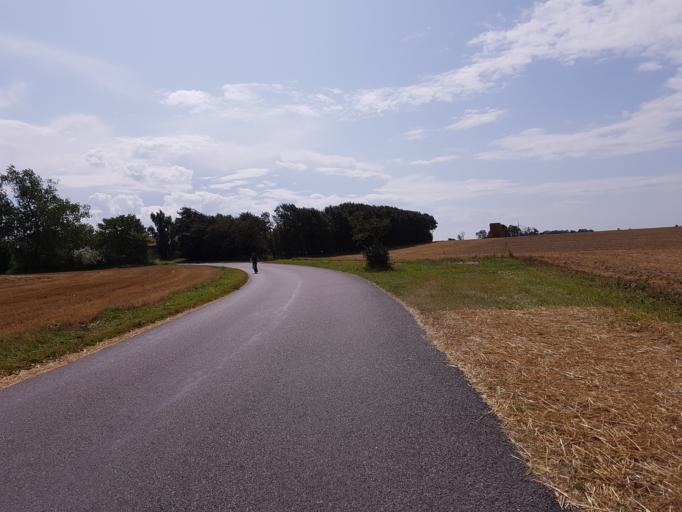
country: DK
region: Zealand
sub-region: Guldborgsund Kommune
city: Nykobing Falster
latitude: 54.5992
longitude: 11.9421
